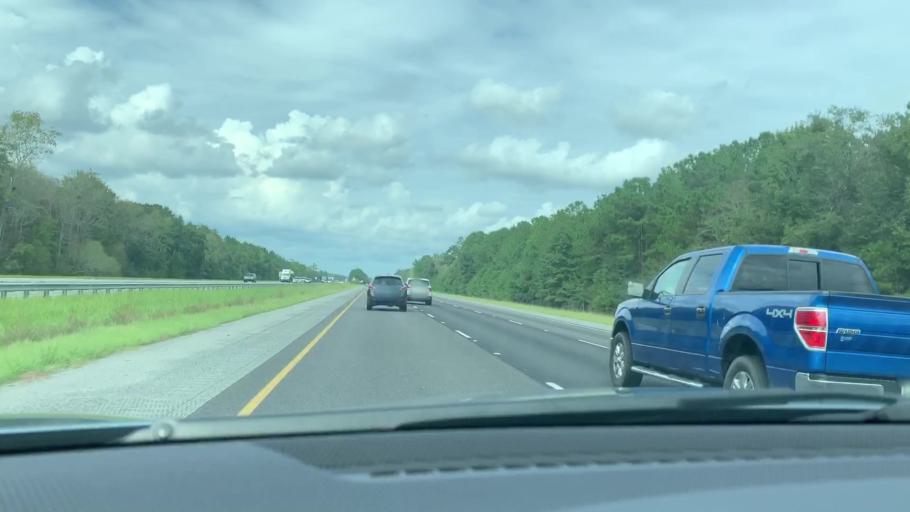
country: US
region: Georgia
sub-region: Liberty County
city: Midway
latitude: 31.6735
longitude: -81.3922
